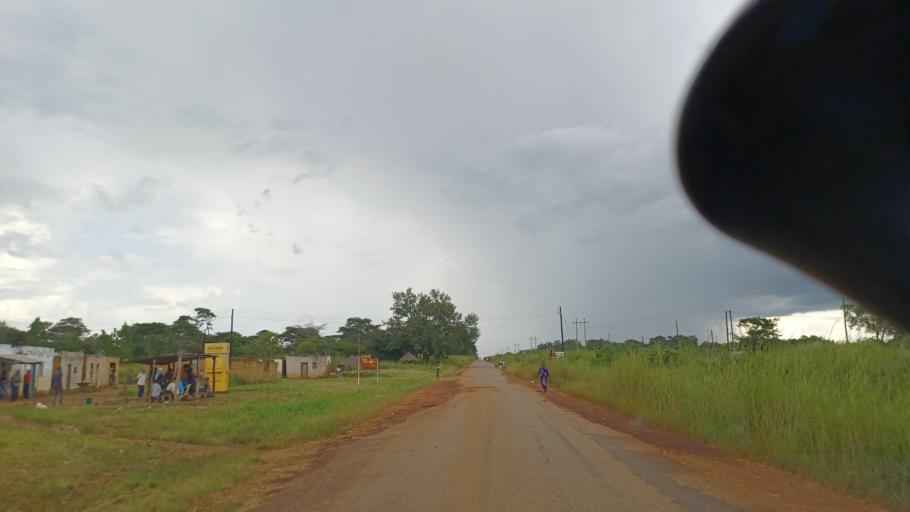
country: ZM
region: North-Western
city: Kasempa
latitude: -13.0163
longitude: 26.0021
